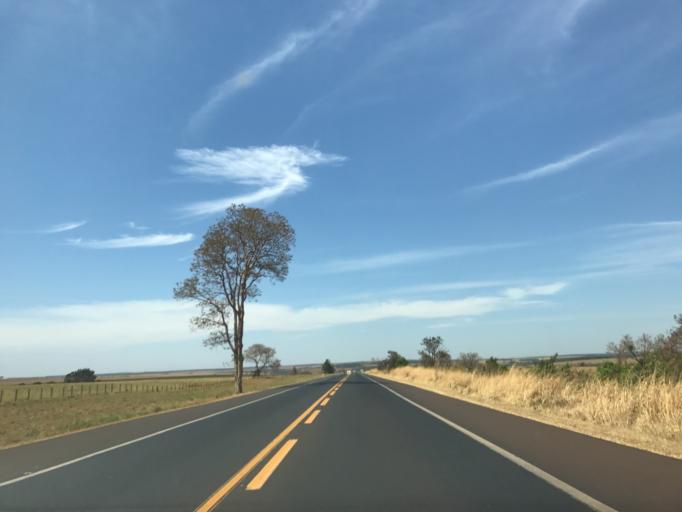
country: BR
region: Minas Gerais
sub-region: Monte Alegre De Minas
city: Monte Alegre de Minas
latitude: -19.0125
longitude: -49.0171
